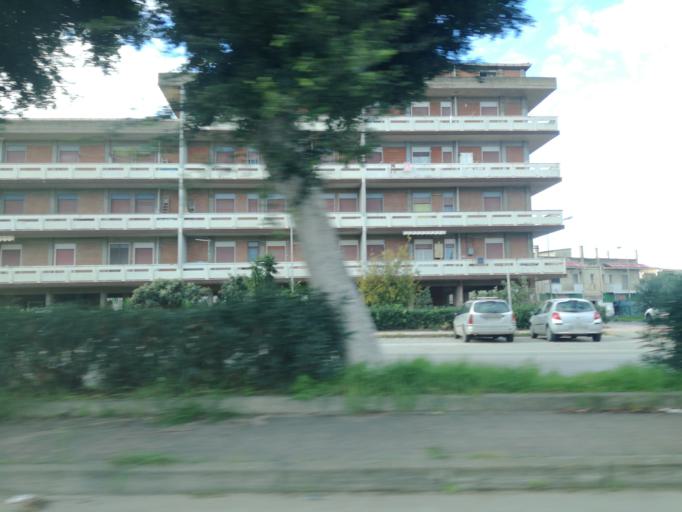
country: IT
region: Sicily
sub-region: Provincia di Caltanissetta
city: Gela
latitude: 37.0774
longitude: 14.2191
